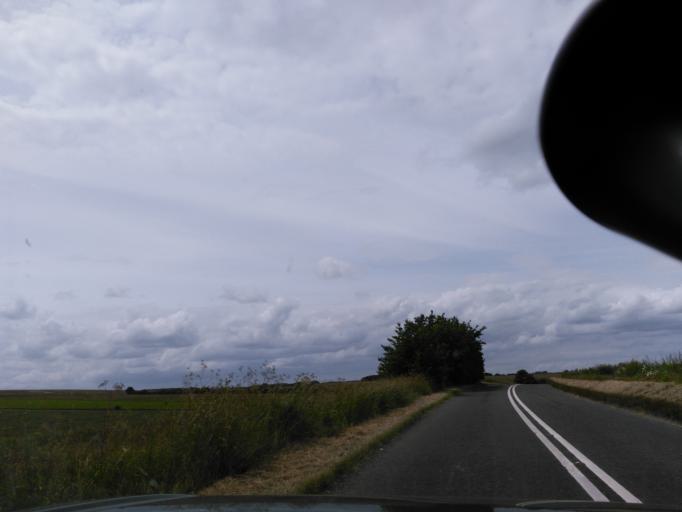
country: GB
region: England
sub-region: Wiltshire
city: Market Lavington
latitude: 51.2310
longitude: -1.9630
